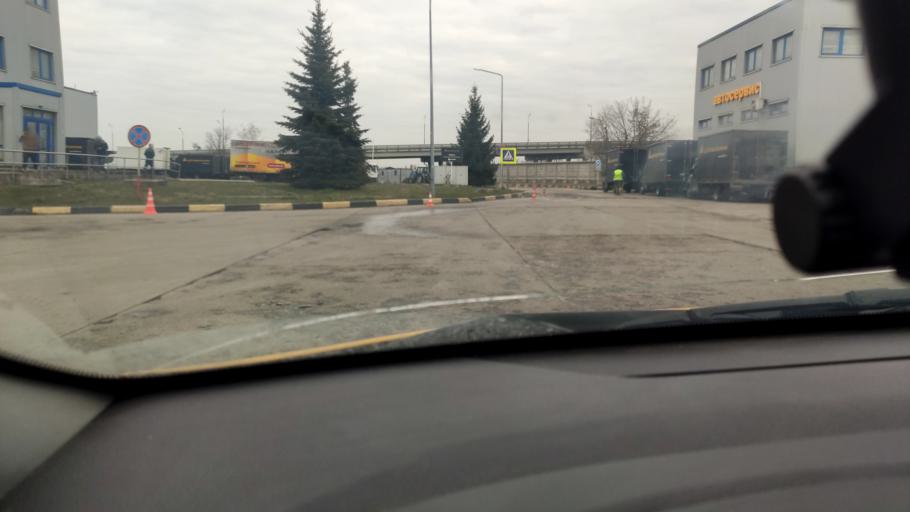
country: RU
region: Moskovskaya
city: Biryulevo Zapadnoye
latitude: 55.5999
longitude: 37.6462
